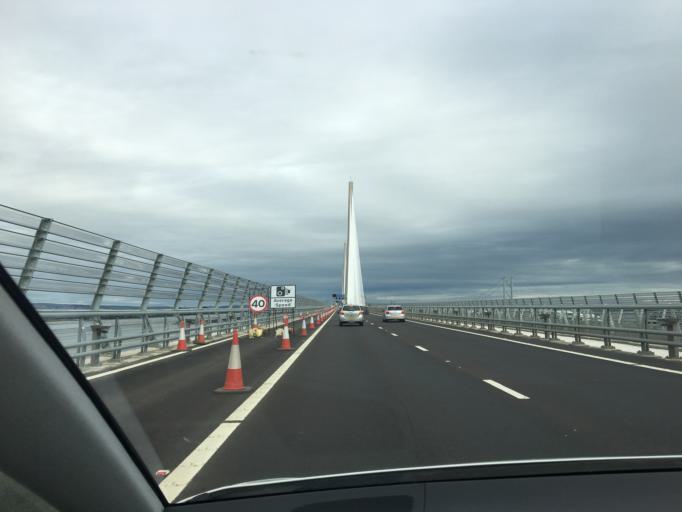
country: GB
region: Scotland
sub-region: Edinburgh
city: Queensferry
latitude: 55.9936
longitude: -3.4198
